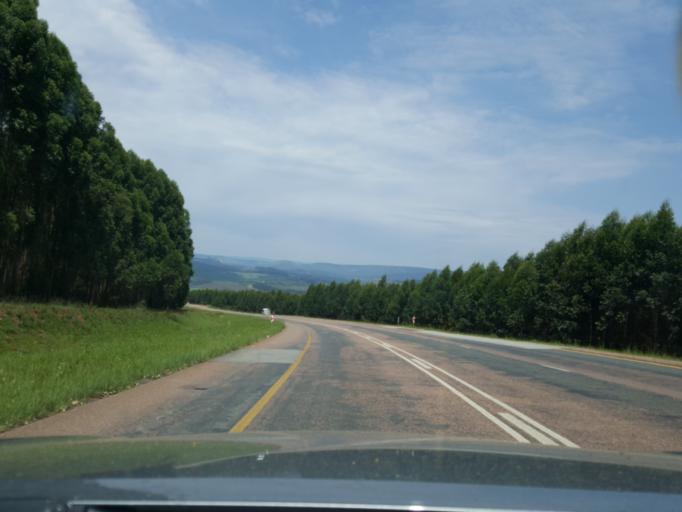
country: ZA
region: Mpumalanga
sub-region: Ehlanzeni District
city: White River
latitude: -25.1942
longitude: 31.0277
